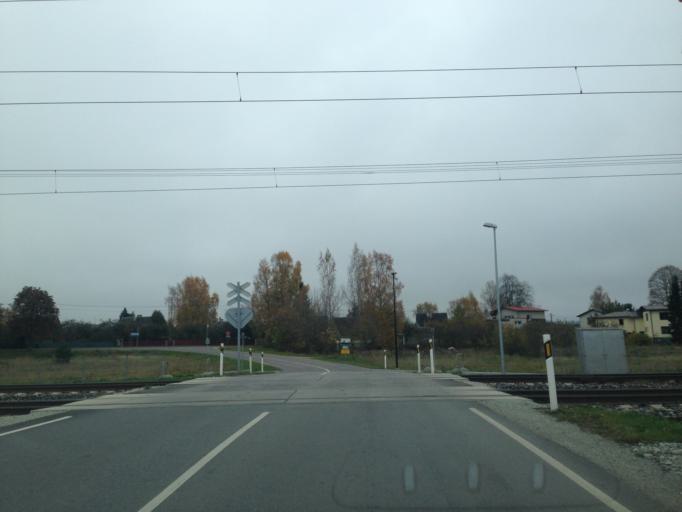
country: EE
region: Harju
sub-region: Saue linn
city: Saue
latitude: 59.3235
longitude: 24.5426
